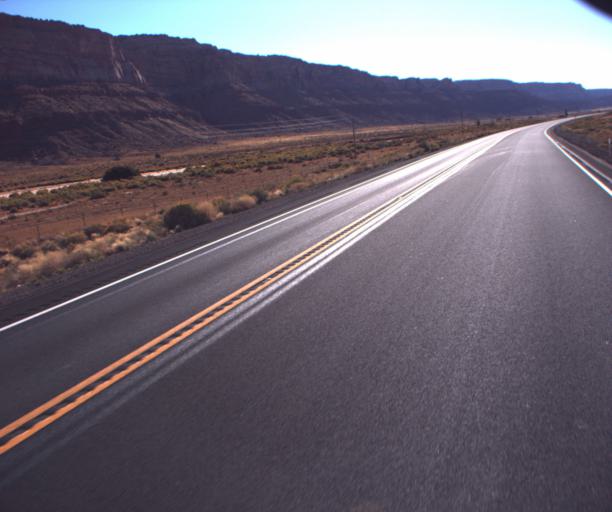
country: US
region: Arizona
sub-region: Coconino County
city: LeChee
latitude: 36.5111
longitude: -111.5874
